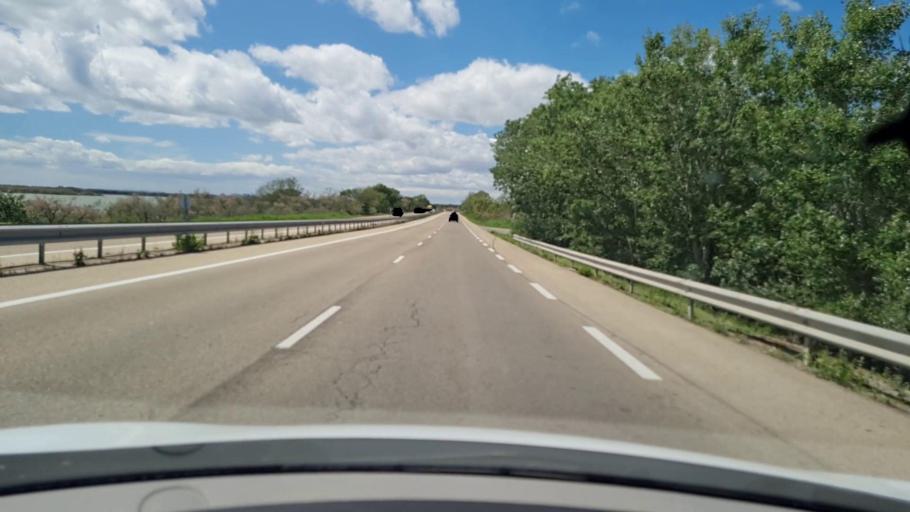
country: FR
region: Languedoc-Roussillon
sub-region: Departement du Gard
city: Le Grau-du-Roi
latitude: 43.5618
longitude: 4.1421
